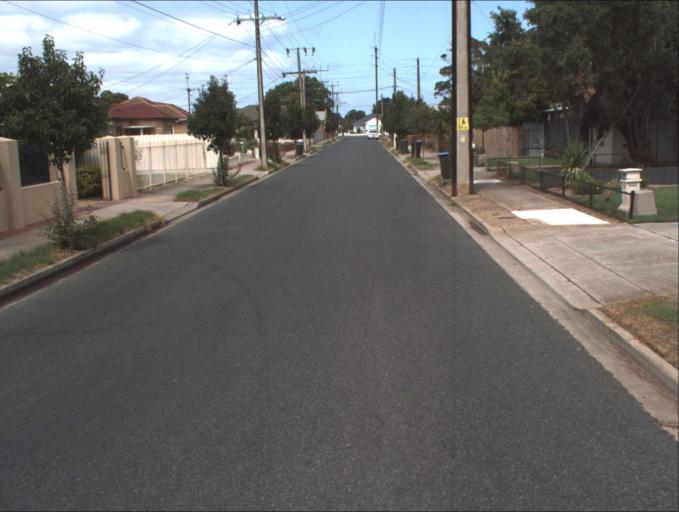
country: AU
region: South Australia
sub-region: Charles Sturt
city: Woodville
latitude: -34.8813
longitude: 138.5620
